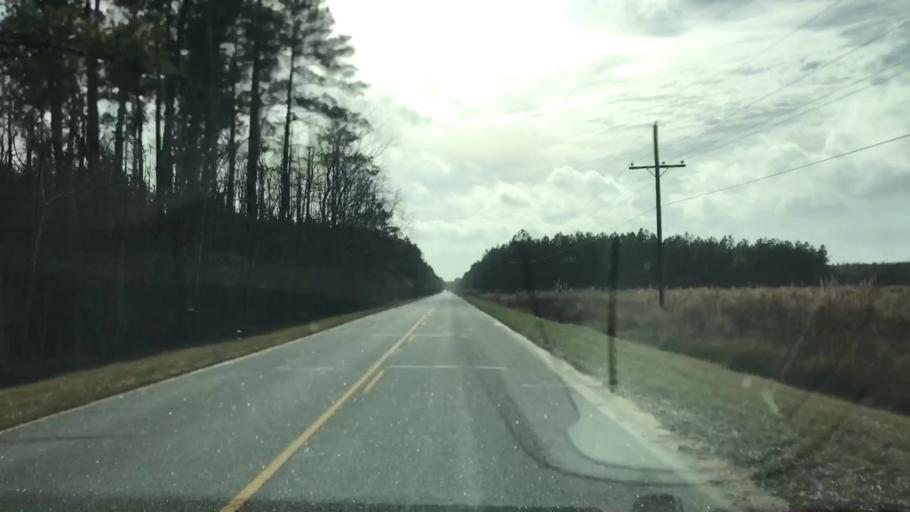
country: US
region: South Carolina
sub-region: Williamsburg County
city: Andrews
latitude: 33.4052
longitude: -79.6118
